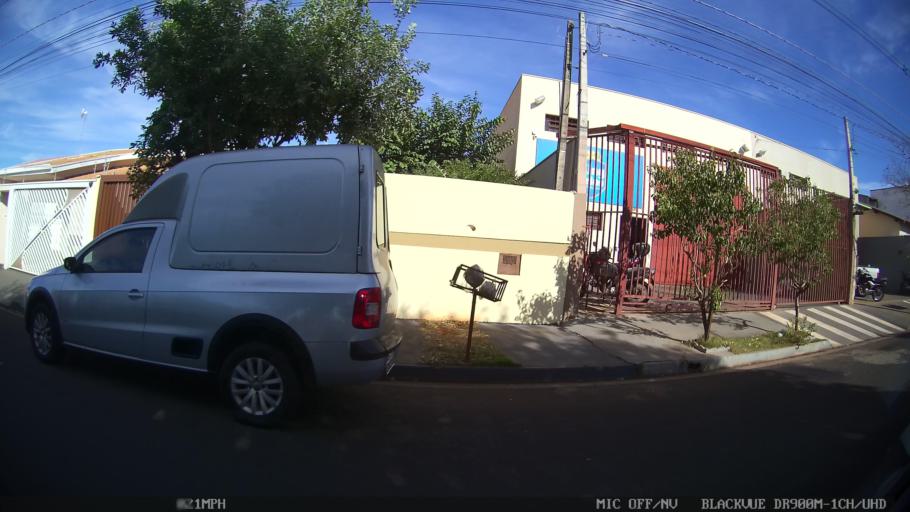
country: BR
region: Sao Paulo
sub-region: Sao Jose Do Rio Preto
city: Sao Jose do Rio Preto
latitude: -20.7848
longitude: -49.3517
